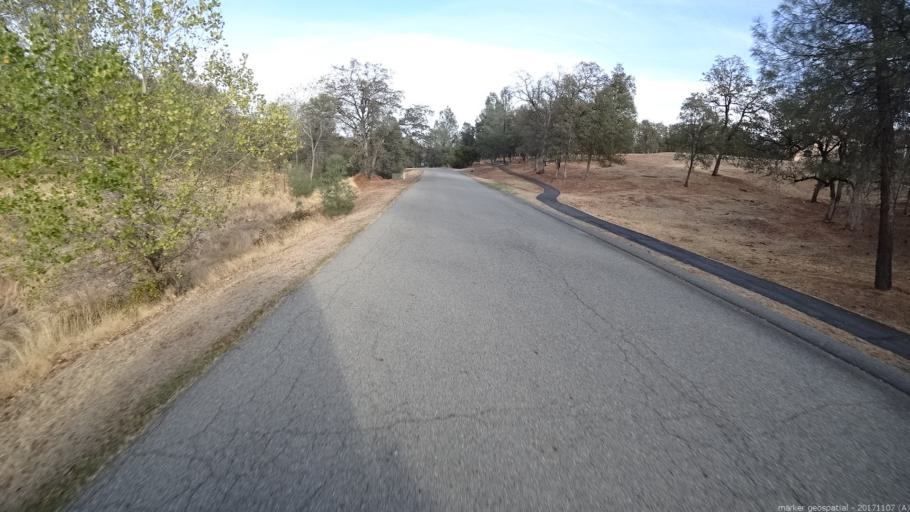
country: US
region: California
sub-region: Shasta County
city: Shasta
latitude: 40.5089
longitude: -122.4725
